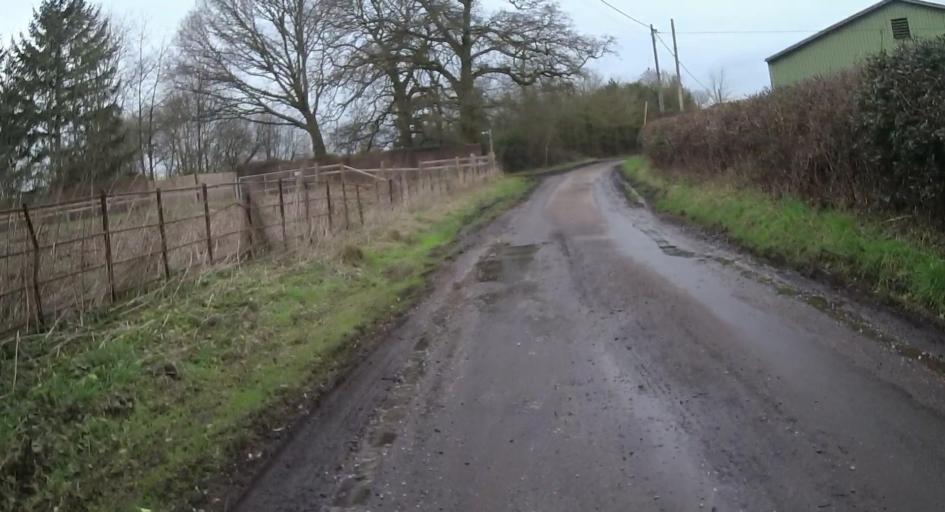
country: GB
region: England
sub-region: West Berkshire
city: Stratfield Mortimer
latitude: 51.3811
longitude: -1.0518
